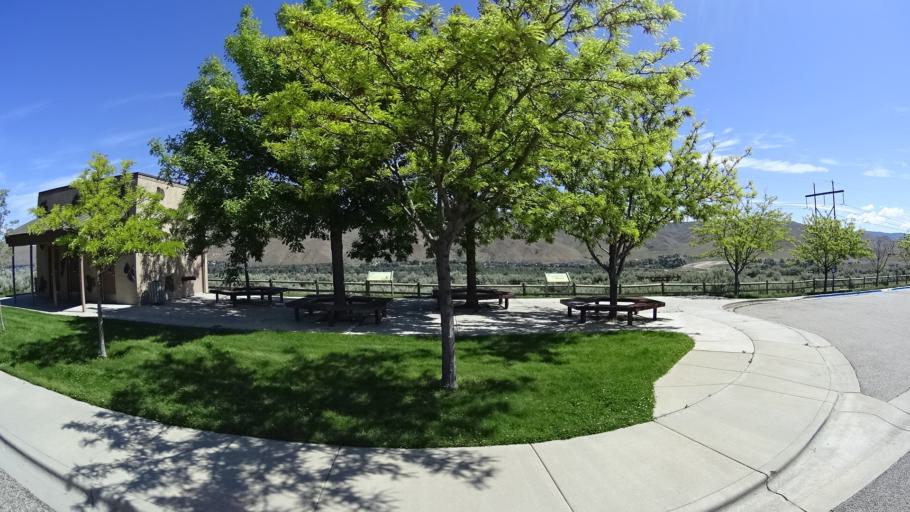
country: US
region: Idaho
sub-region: Ada County
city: Boise
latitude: 43.5466
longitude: -116.1156
